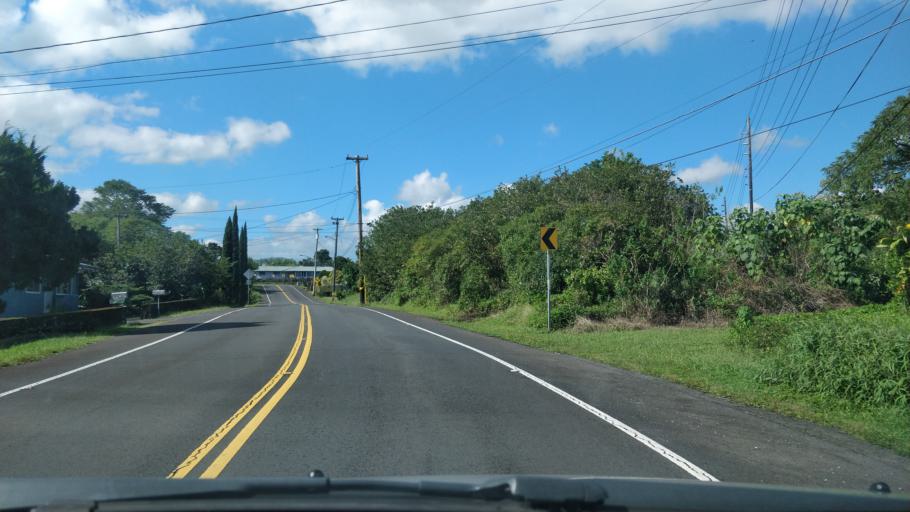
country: US
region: Hawaii
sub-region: Hawaii County
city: Hilo
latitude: 19.6820
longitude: -155.1049
